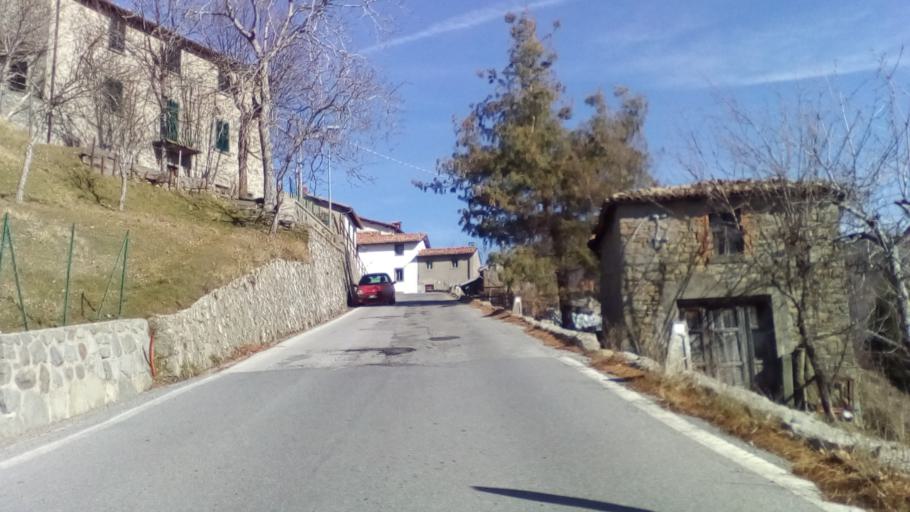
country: IT
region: Tuscany
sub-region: Provincia di Lucca
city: Castiglione di Garfagnana
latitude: 44.1571
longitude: 10.4389
